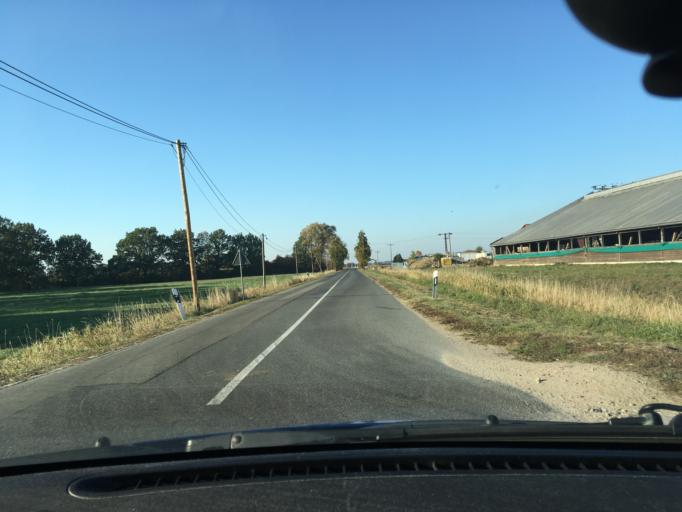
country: DE
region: Lower Saxony
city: Hitzacker
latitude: 53.1563
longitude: 11.0752
